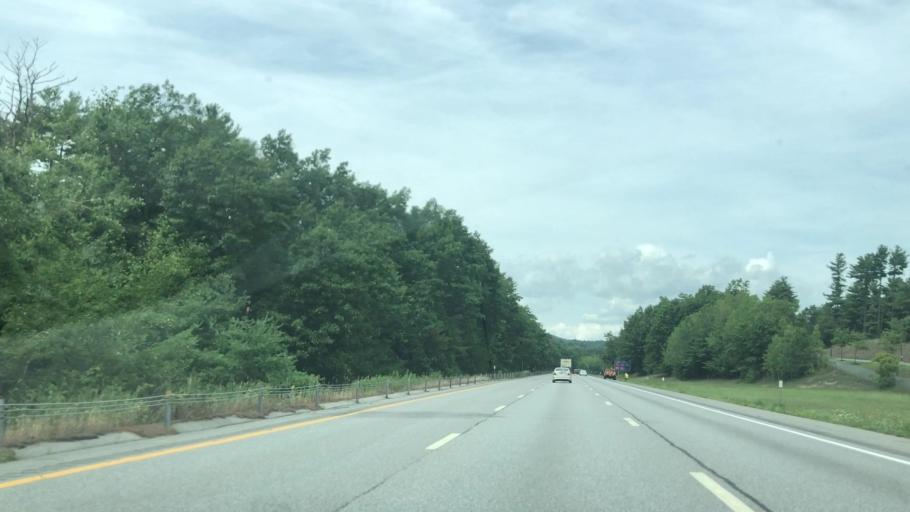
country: US
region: New York
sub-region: Warren County
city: Glens Falls North
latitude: 43.3525
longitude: -73.6989
